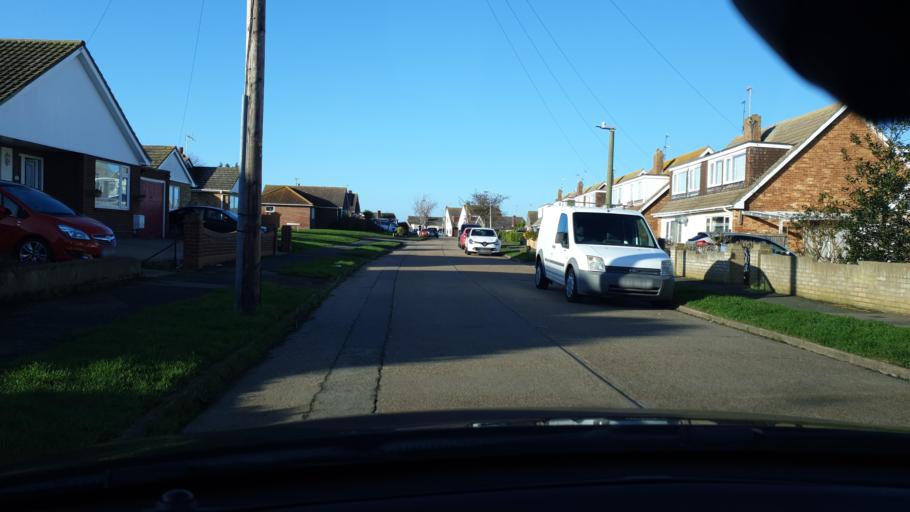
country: GB
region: England
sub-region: Essex
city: Clacton-on-Sea
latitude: 51.8093
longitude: 1.1963
